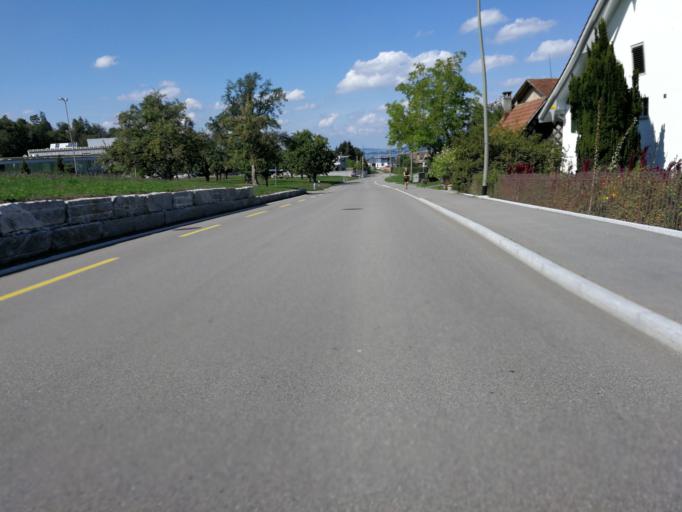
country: CH
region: Zurich
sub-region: Bezirk Horgen
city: Horgen / Allmend
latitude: 47.2489
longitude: 8.6194
